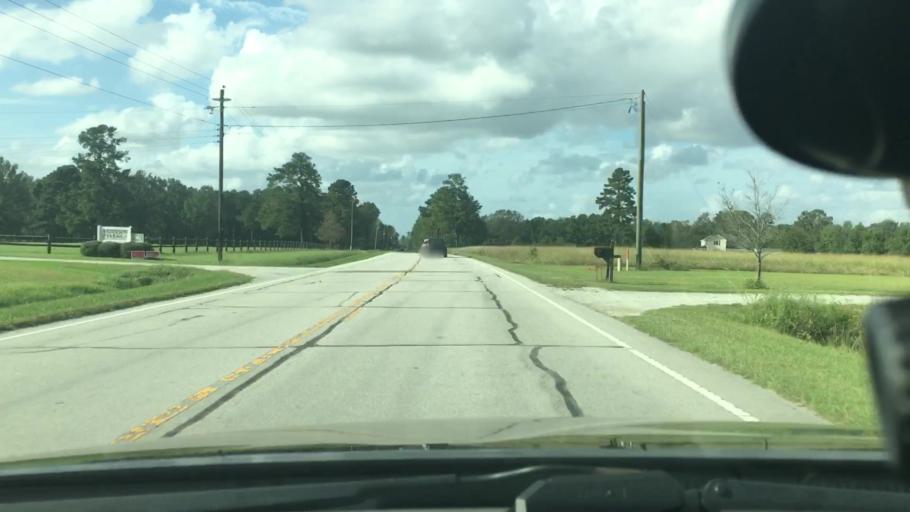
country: US
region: North Carolina
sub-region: Craven County
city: Vanceboro
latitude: 35.3195
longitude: -77.1643
